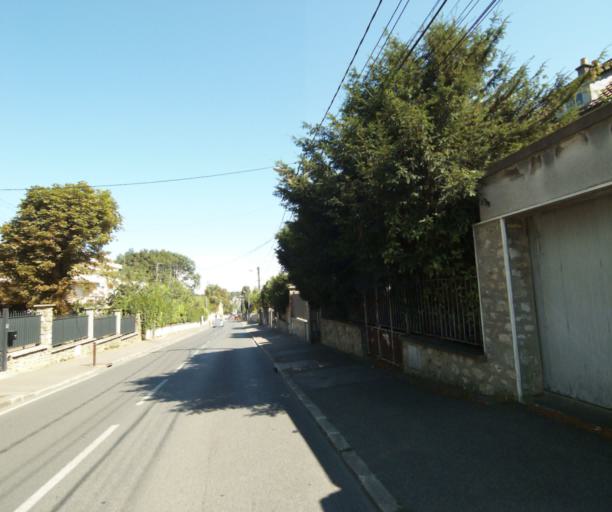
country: FR
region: Ile-de-France
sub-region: Departement de Seine-et-Marne
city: Lagny-sur-Marne
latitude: 48.8715
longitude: 2.7066
